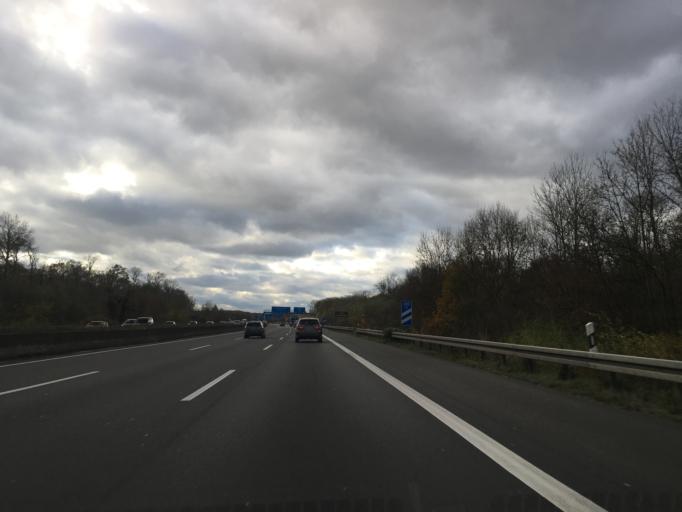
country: DE
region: North Rhine-Westphalia
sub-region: Regierungsbezirk Koln
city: Kerpen
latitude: 50.9003
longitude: 6.7065
